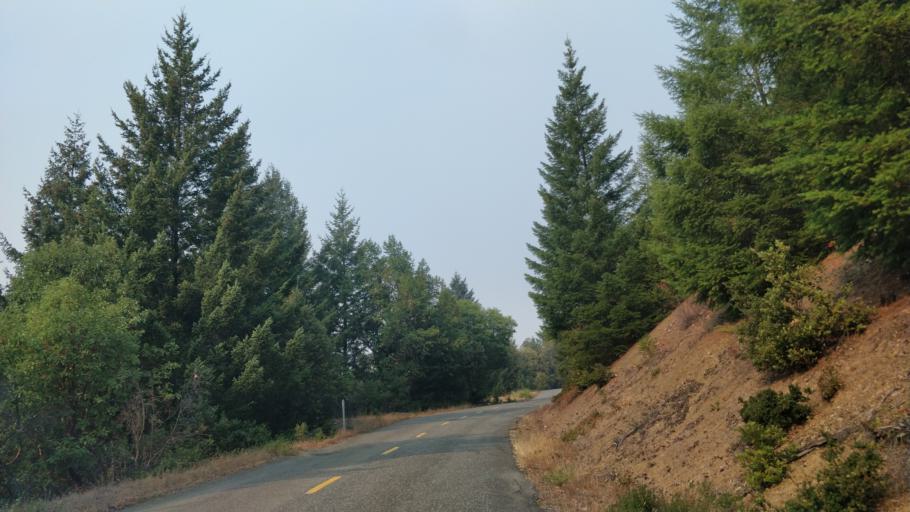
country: US
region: California
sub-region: Humboldt County
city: Rio Dell
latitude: 40.2564
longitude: -124.1176
